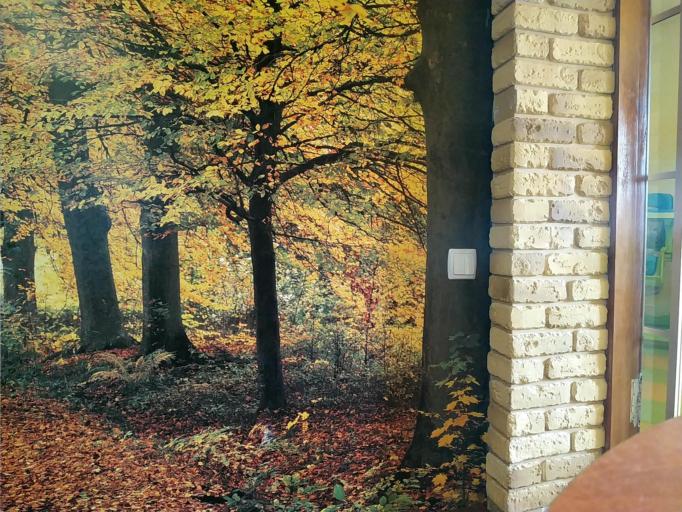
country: RU
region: Smolensk
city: Katyn'
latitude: 54.8892
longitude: 31.7961
